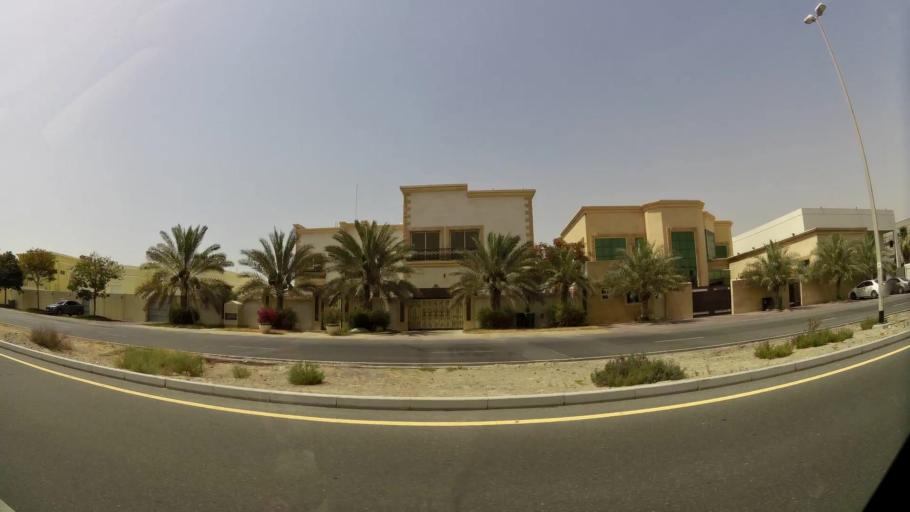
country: AE
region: Ash Shariqah
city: Sharjah
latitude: 25.2482
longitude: 55.4276
